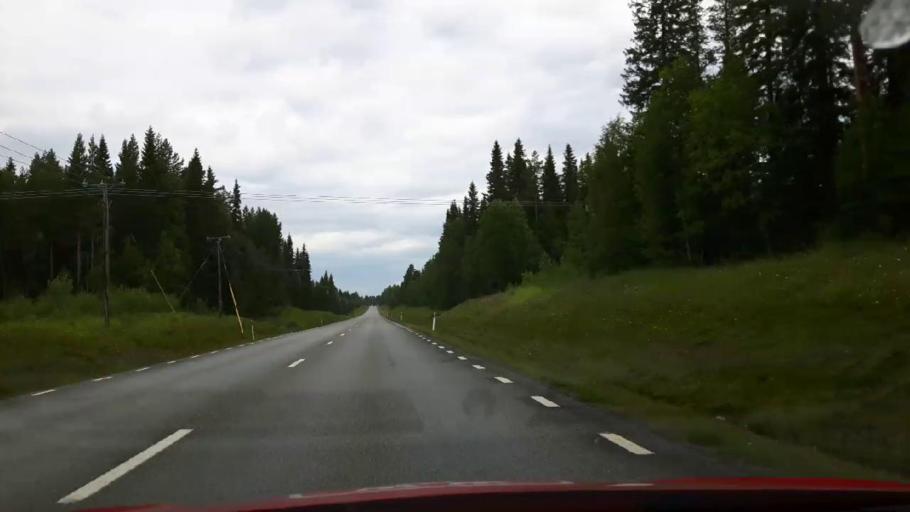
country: SE
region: Jaemtland
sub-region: Stroemsunds Kommun
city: Stroemsund
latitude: 63.6210
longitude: 15.3556
